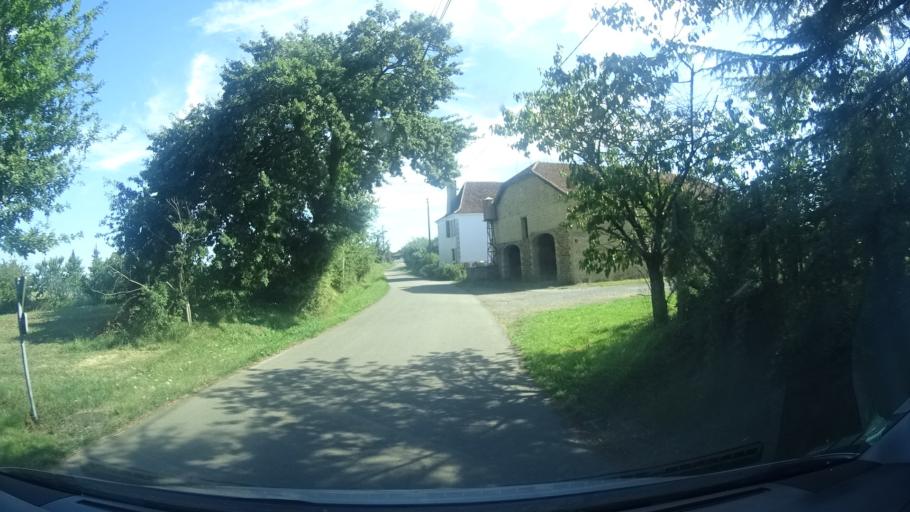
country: FR
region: Aquitaine
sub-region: Departement des Pyrenees-Atlantiques
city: Mont
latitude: 43.4914
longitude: -0.6638
